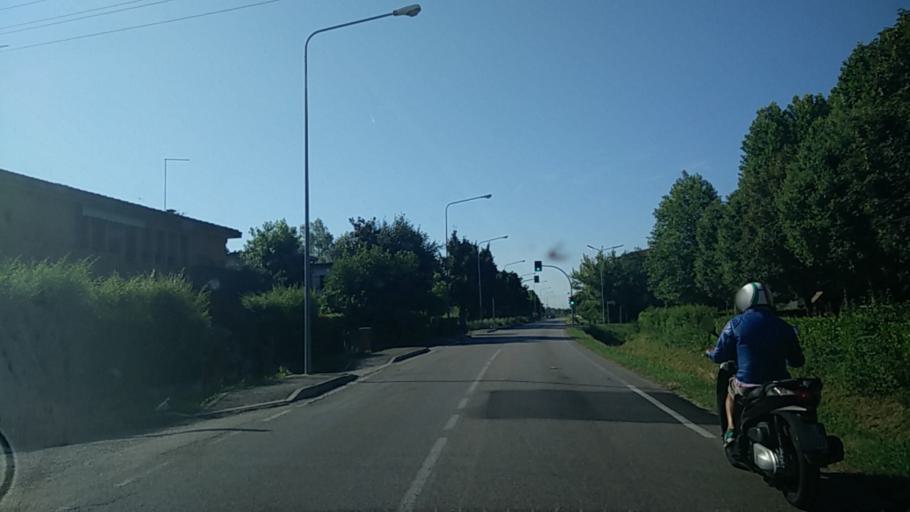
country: IT
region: Veneto
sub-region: Provincia di Venezia
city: Dolo
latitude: 45.4192
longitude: 12.0804
